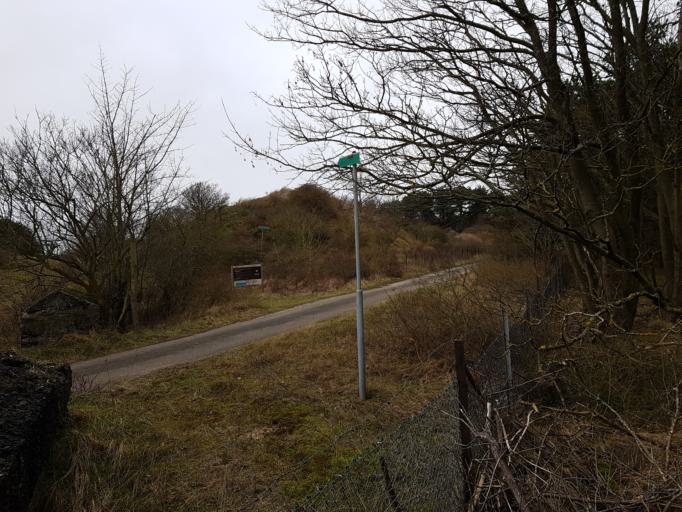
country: NL
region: North Holland
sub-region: Gemeente Zandvoort
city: Zandvoort
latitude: 52.3979
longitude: 4.5618
